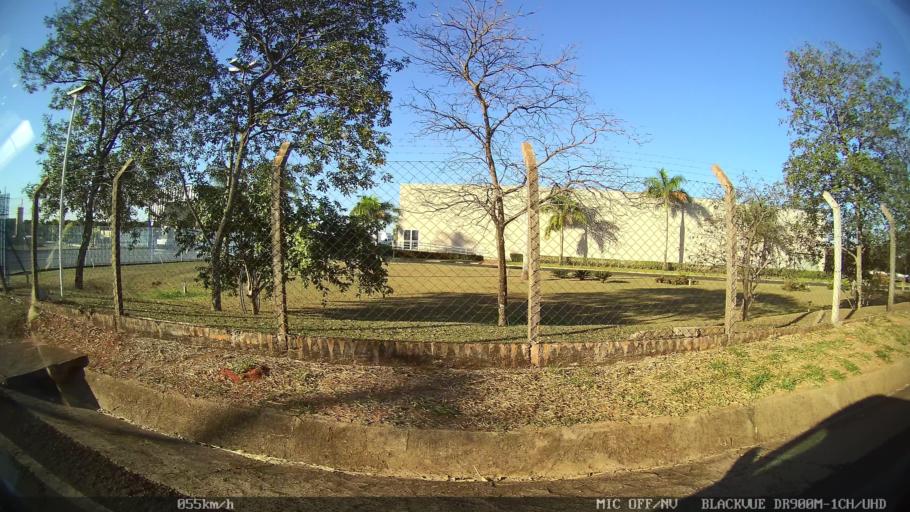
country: BR
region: Sao Paulo
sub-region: Guapiacu
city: Guapiacu
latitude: -20.7827
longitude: -49.2591
